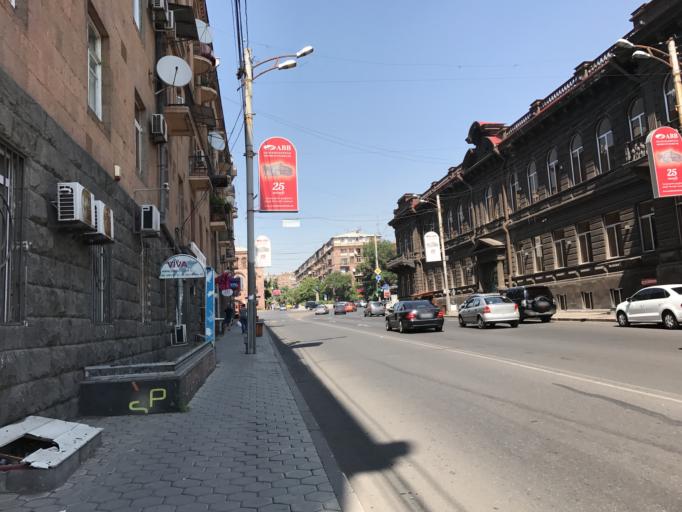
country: AM
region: Yerevan
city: Yerevan
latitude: 40.1792
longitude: 44.5158
